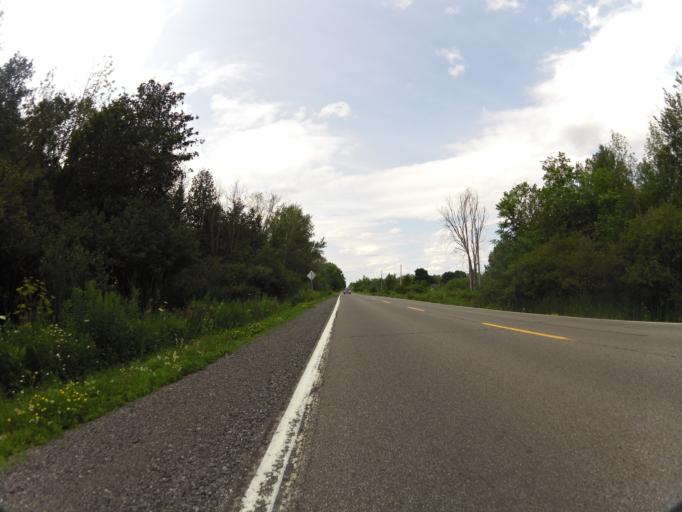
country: CA
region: Ontario
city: Ottawa
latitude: 45.2082
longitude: -75.5960
